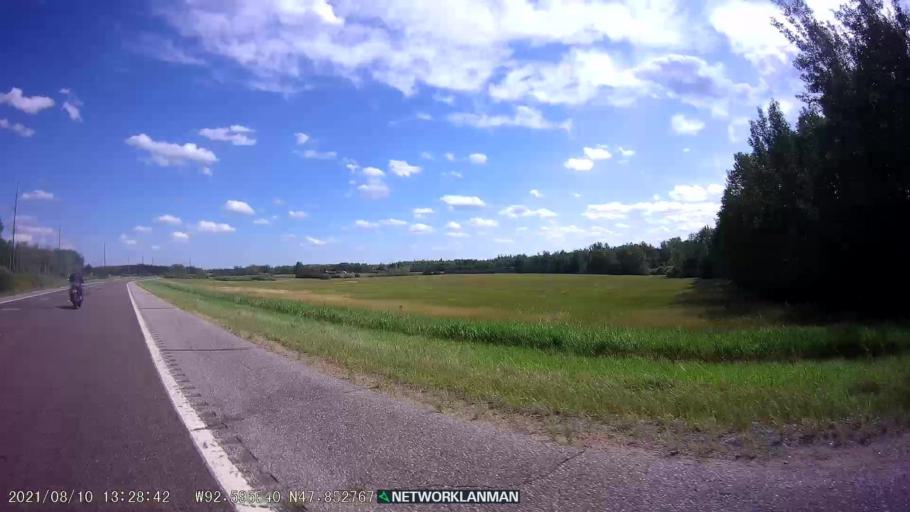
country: US
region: Minnesota
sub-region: Saint Louis County
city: Mountain Iron
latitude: 47.8526
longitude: -92.5950
